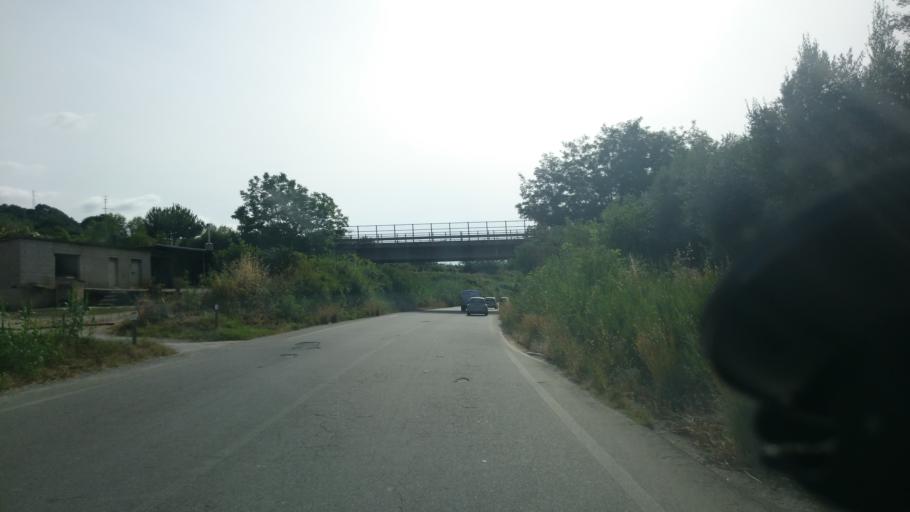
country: IT
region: Calabria
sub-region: Provincia di Vibo-Valentia
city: Stefanaconi
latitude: 38.7065
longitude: 16.1123
